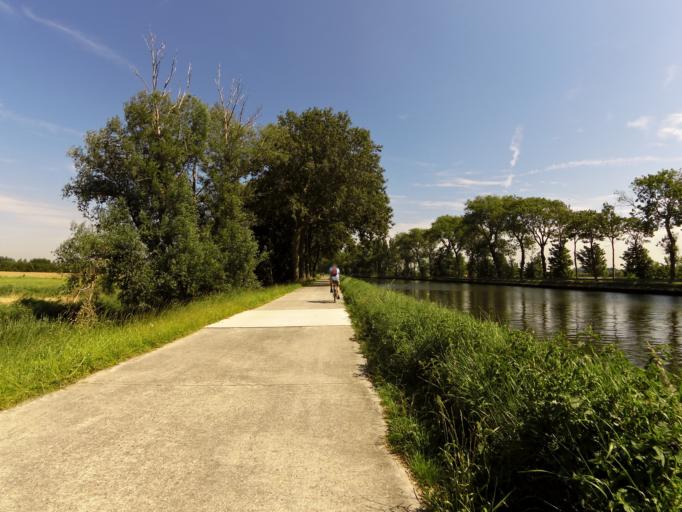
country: BE
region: Flanders
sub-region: Provincie West-Vlaanderen
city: Jabbeke
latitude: 51.2018
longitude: 3.0666
